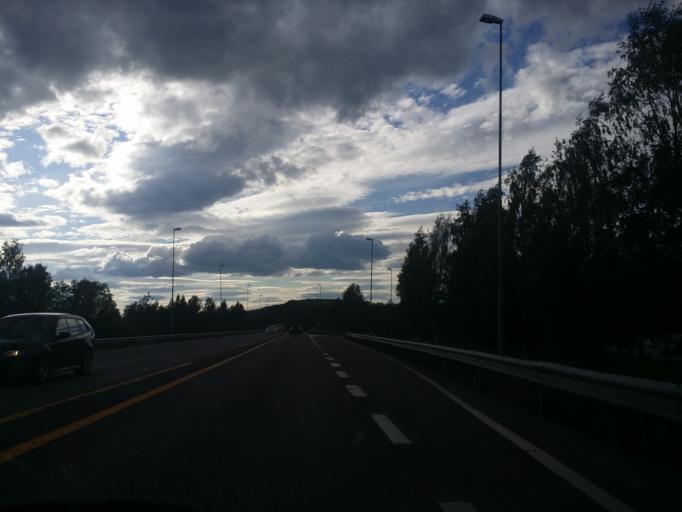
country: NO
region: Hedmark
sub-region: Ringsaker
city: Brumunddal
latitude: 60.8779
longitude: 10.9318
